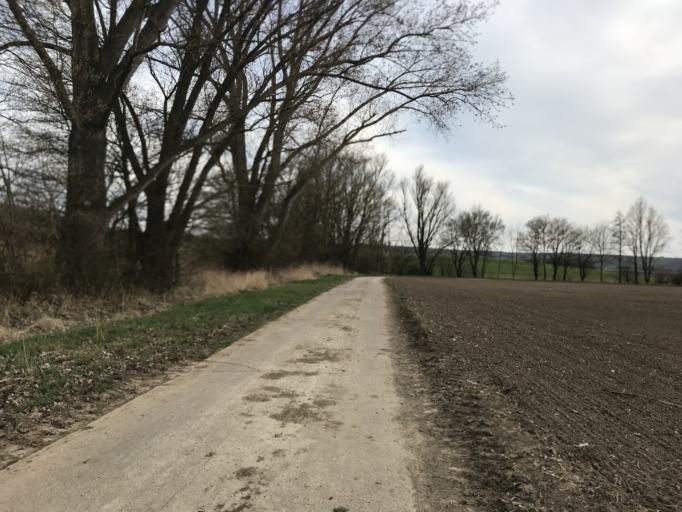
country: DE
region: Rheinland-Pfalz
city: Stadecken-Elsheim
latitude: 49.8986
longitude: 8.1236
